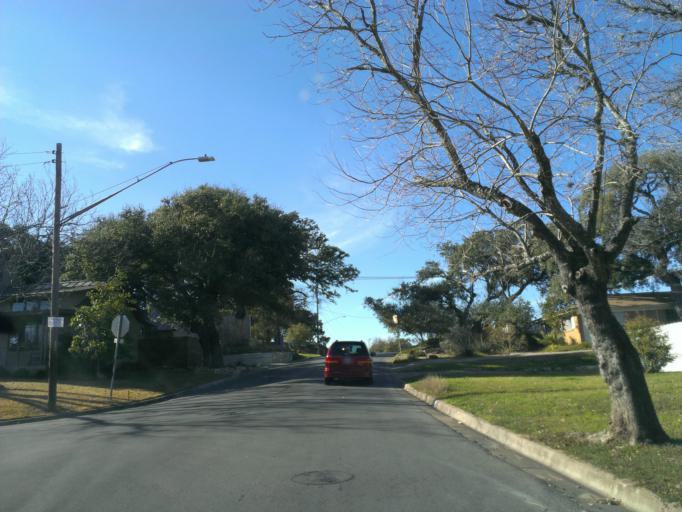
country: US
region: Texas
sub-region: Travis County
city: Austin
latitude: 30.2358
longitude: -97.7523
